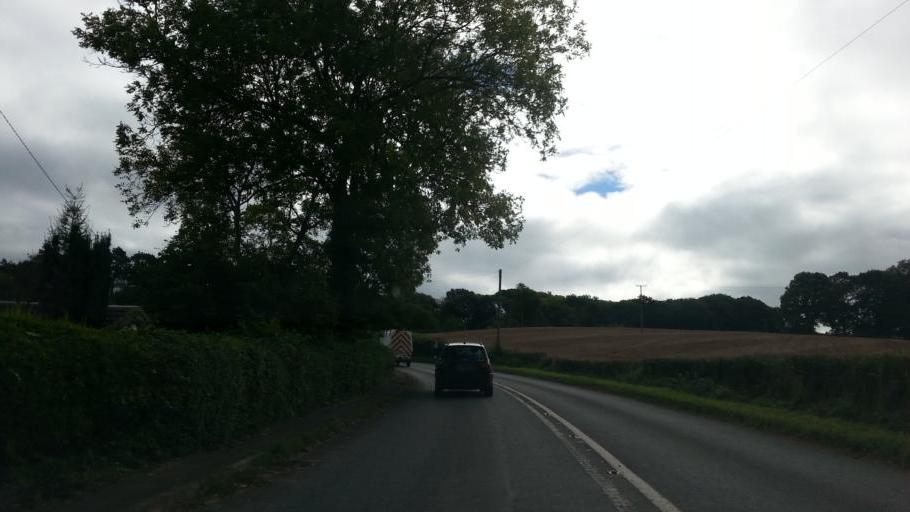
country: GB
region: England
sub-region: Herefordshire
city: Lea
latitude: 51.8895
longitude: -2.4868
